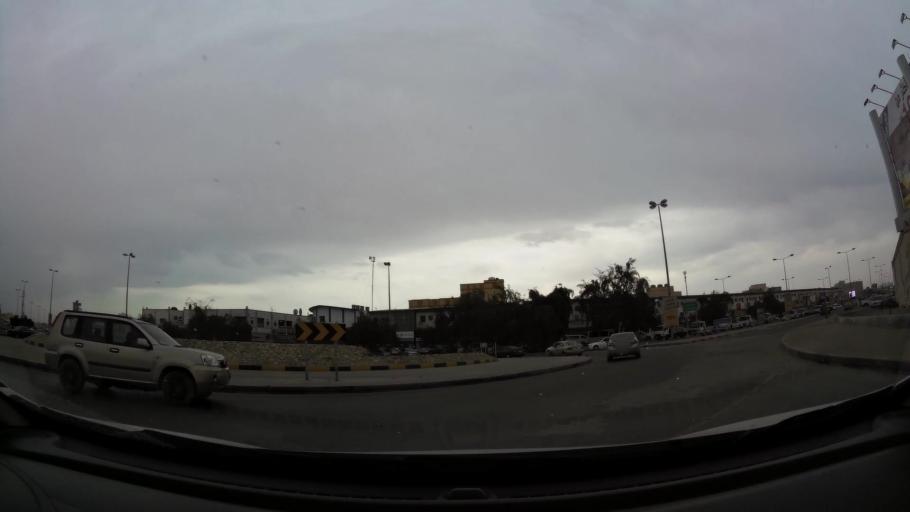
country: BH
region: Central Governorate
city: Madinat Hamad
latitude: 26.1442
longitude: 50.4926
